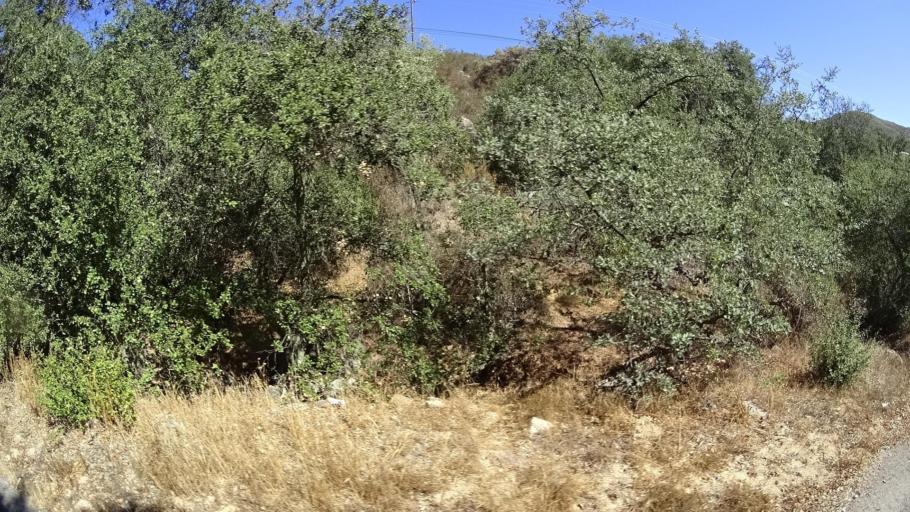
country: US
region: California
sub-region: San Diego County
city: Alpine
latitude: 32.7104
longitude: -116.7423
